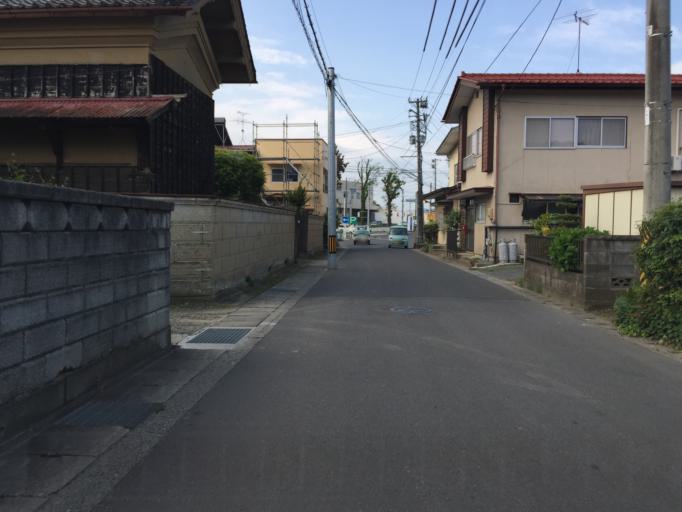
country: JP
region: Fukushima
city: Yanagawamachi-saiwaicho
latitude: 37.8582
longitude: 140.6066
